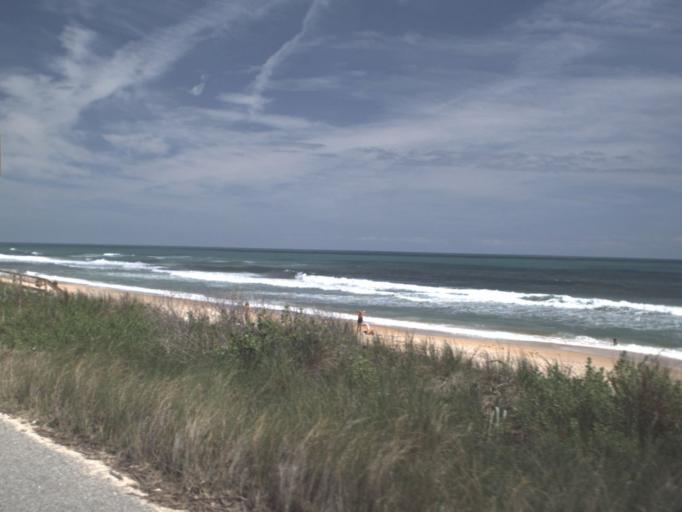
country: US
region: Florida
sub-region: Flagler County
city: Flagler Beach
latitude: 29.4344
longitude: -81.1059
